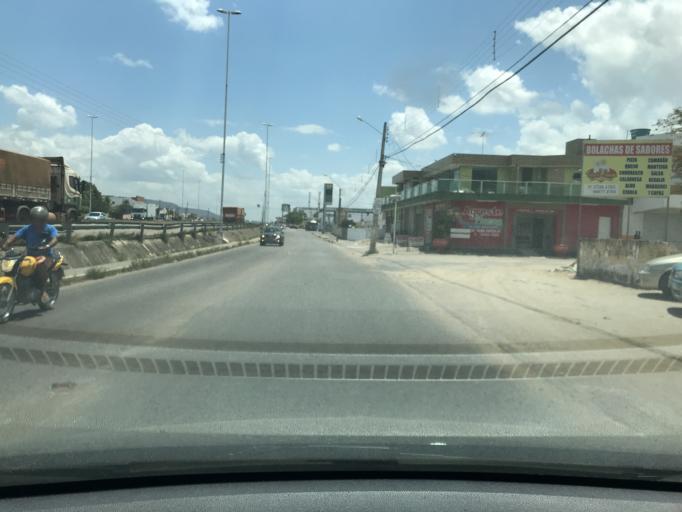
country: BR
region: Pernambuco
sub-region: Bezerros
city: Bezerros
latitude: -8.2388
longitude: -35.7465
